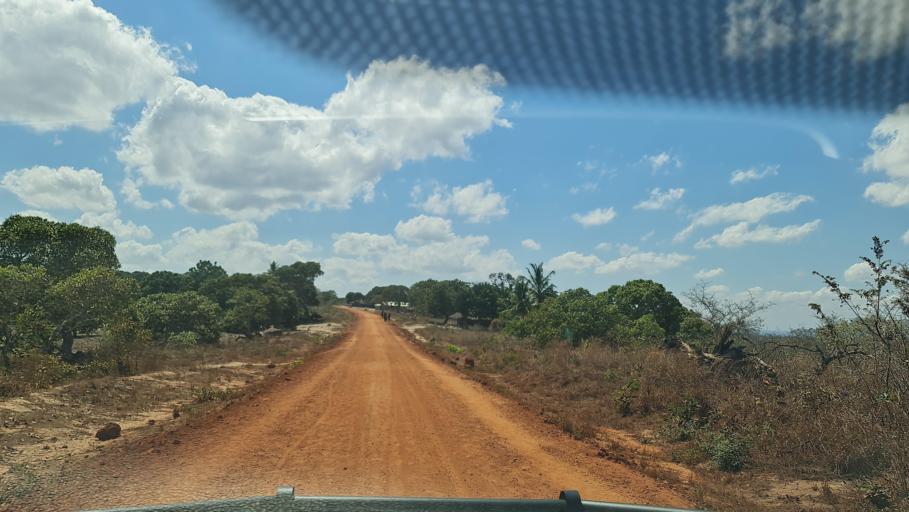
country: MZ
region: Nampula
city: Nacala
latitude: -14.1758
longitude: 40.2082
